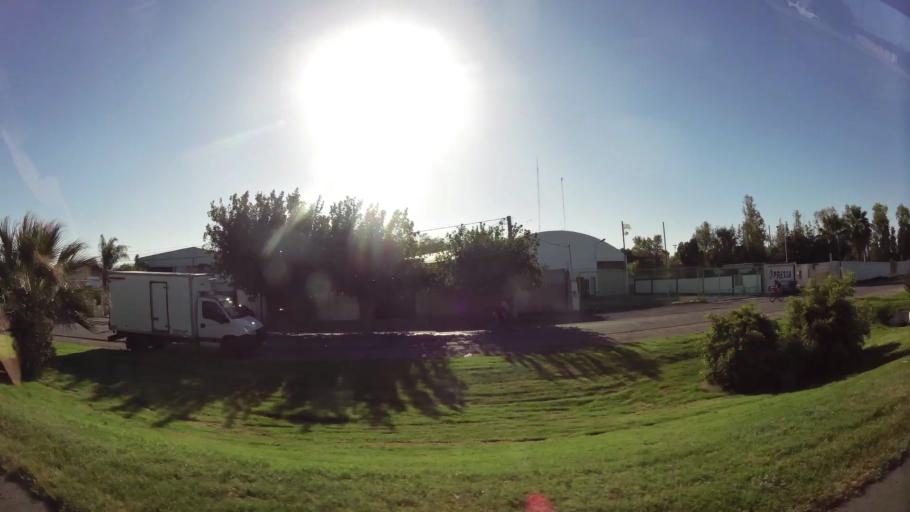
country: AR
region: San Juan
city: Villa Krause
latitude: -31.5711
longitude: -68.5176
